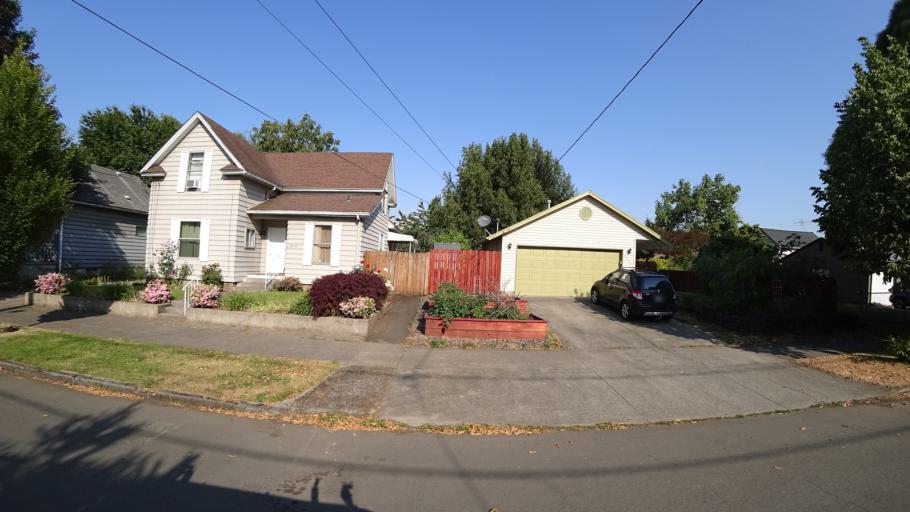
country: US
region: Oregon
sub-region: Washington County
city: West Haven
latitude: 45.5908
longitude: -122.7455
